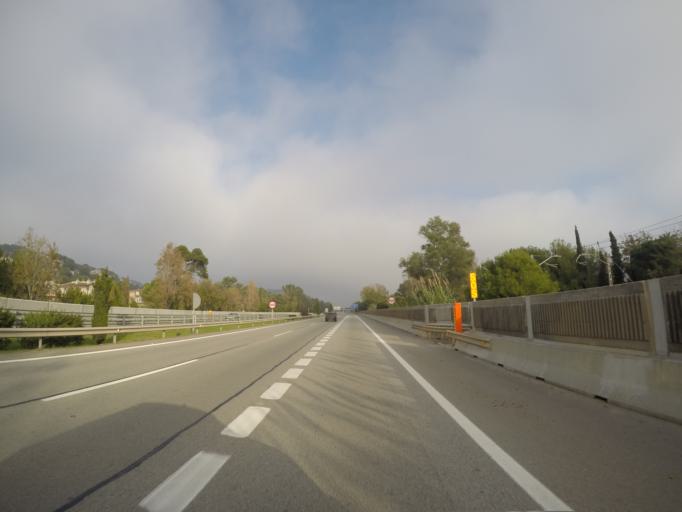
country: ES
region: Catalonia
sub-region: Provincia de Barcelona
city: Castelldefels
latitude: 41.2660
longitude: 1.9460
